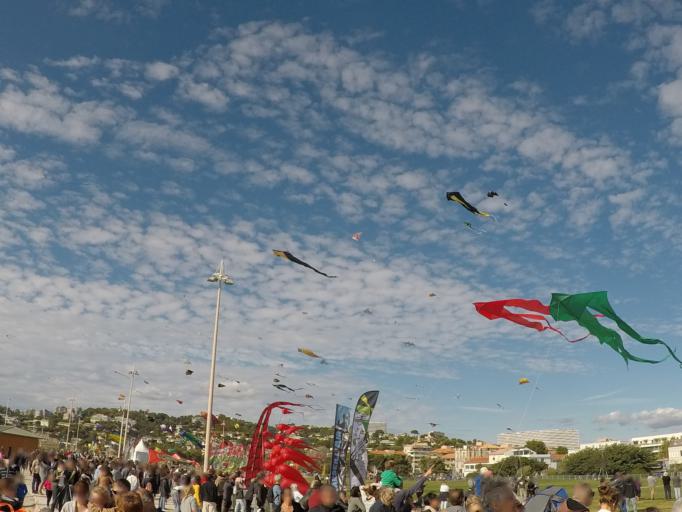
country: FR
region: Provence-Alpes-Cote d'Azur
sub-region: Departement des Bouches-du-Rhone
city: Marseille 08
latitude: 43.2613
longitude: 5.3729
